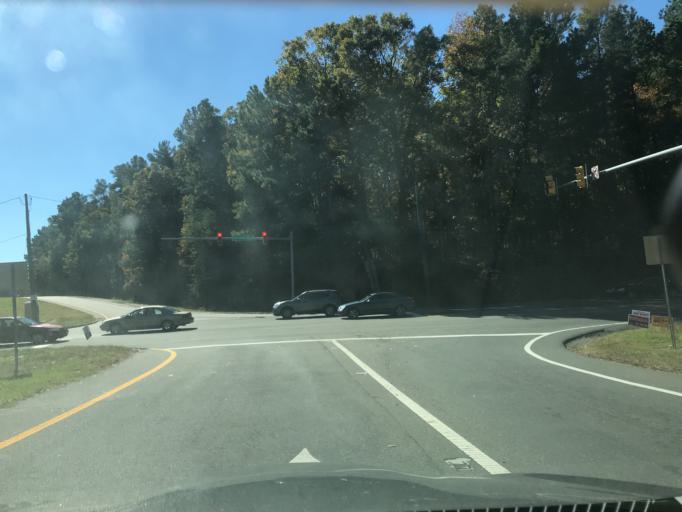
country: US
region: North Carolina
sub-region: Durham County
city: Durham
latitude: 35.9991
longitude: -78.9589
